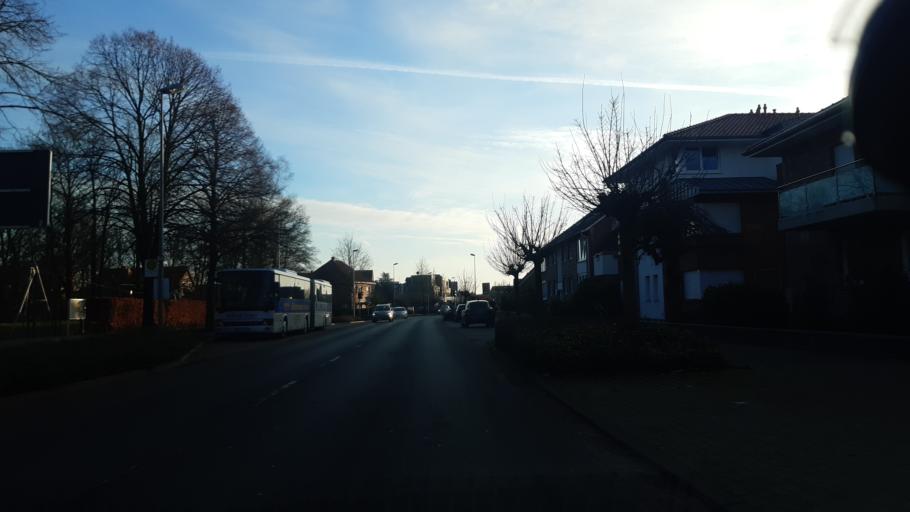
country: DE
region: Lower Saxony
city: Cloppenburg
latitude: 52.8502
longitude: 8.0371
